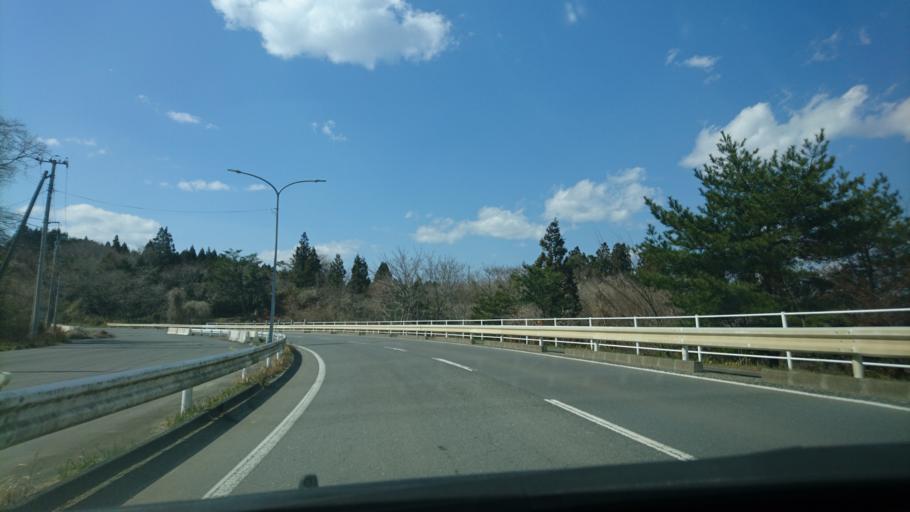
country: JP
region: Miyagi
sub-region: Oshika Gun
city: Onagawa Cho
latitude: 38.6392
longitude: 141.4984
